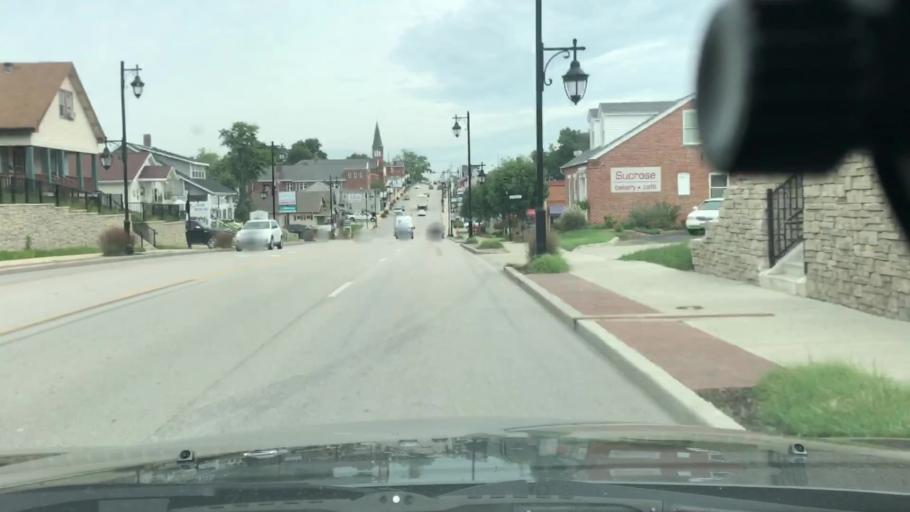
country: US
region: Missouri
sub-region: Saint Charles County
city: Saint Charles
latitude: 38.7774
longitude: -90.4888
